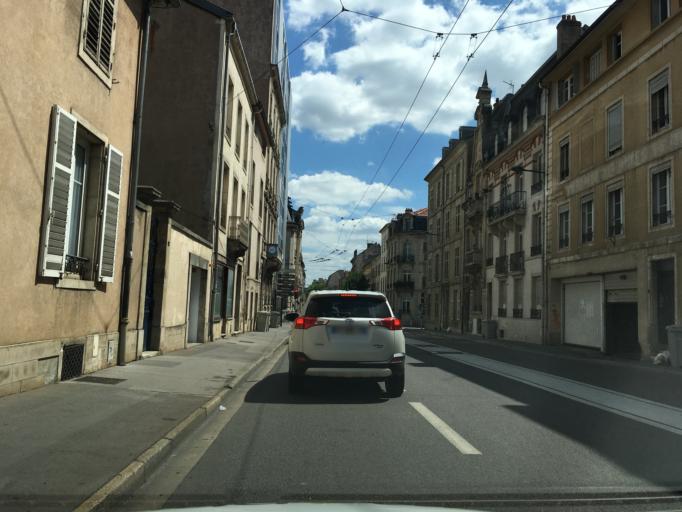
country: FR
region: Lorraine
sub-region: Departement de Meurthe-et-Moselle
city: Nancy
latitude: 48.6882
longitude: 6.1705
